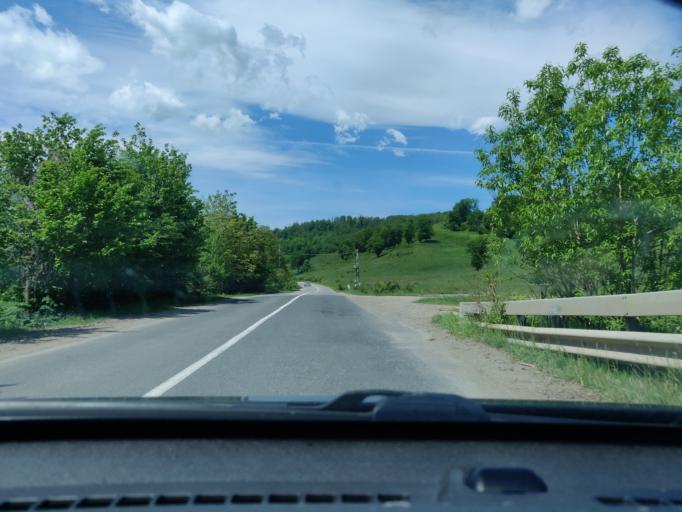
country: RO
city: Campurile de Jos
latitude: 46.0419
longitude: 26.7221
